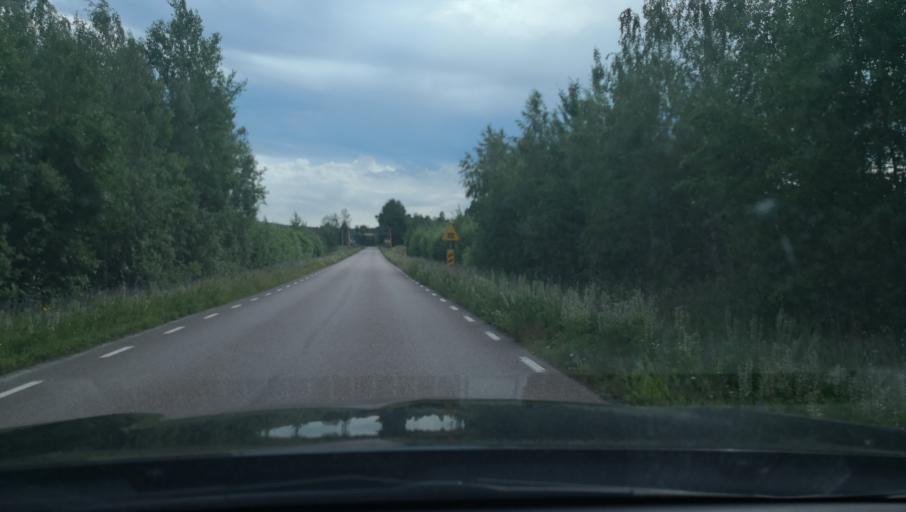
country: SE
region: Dalarna
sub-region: Smedjebackens Kommun
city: Smedjebacken
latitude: 60.0523
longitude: 15.5571
